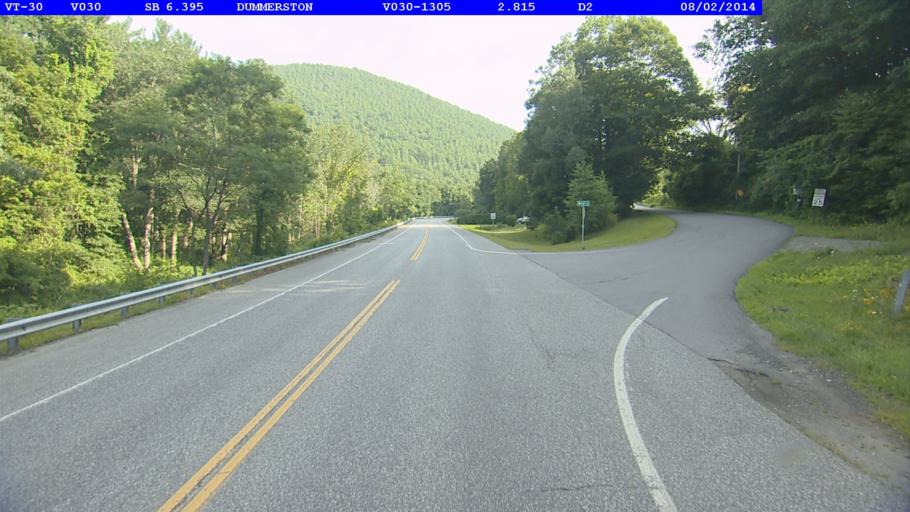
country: US
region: Vermont
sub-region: Windham County
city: Newfane
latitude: 42.9329
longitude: -72.6123
